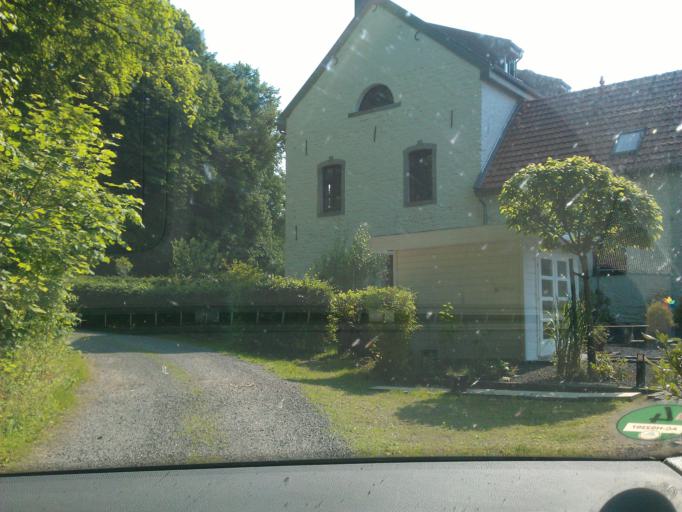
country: DE
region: North Rhine-Westphalia
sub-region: Regierungsbezirk Koln
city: Aachen
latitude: 50.7951
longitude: 6.0555
